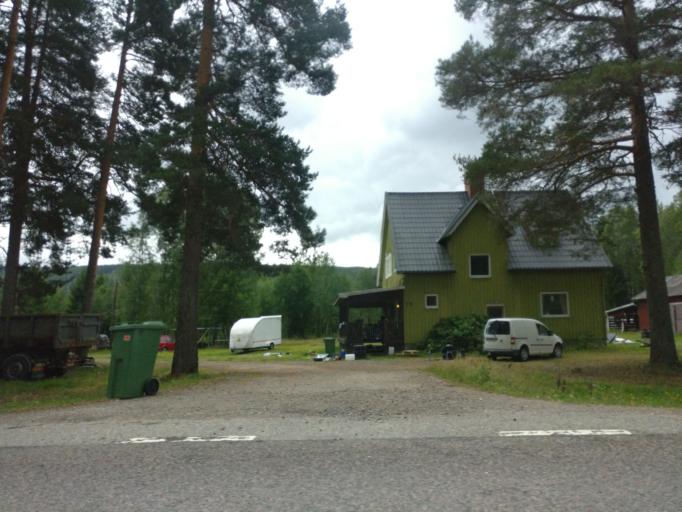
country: SE
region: Vaermland
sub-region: Torsby Kommun
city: Torsby
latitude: 60.7527
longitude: 12.7831
